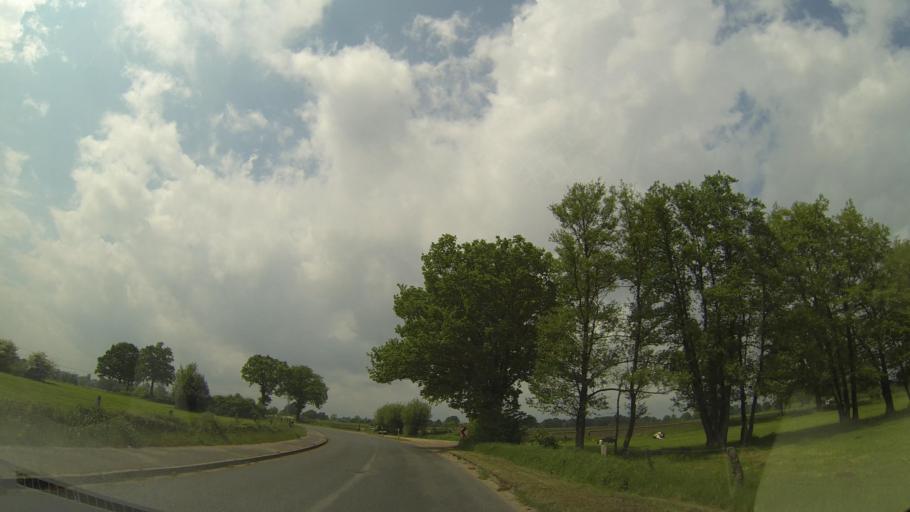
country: DE
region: Schleswig-Holstein
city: Tangstedt
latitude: 53.6616
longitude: 9.8615
